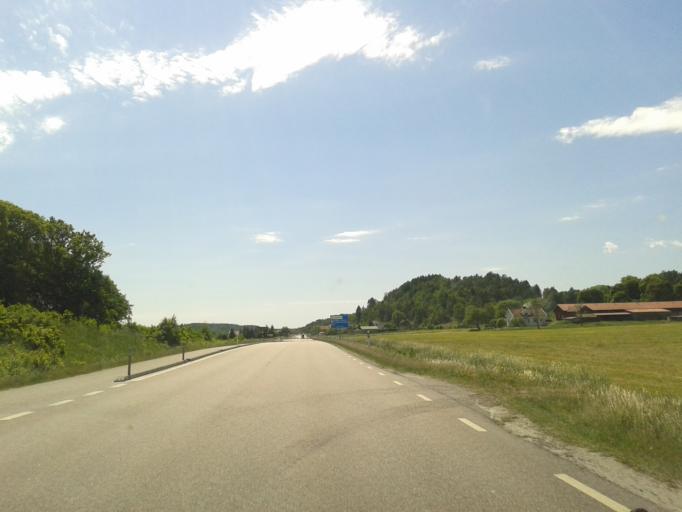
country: SE
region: Vaestra Goetaland
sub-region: Stenungsunds Kommun
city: Stora Hoga
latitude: 58.0329
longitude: 11.8772
